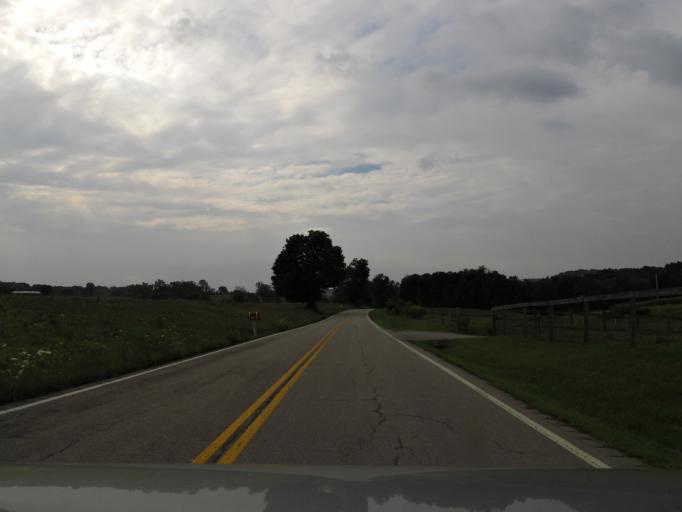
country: US
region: Kentucky
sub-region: Robertson County
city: Mount Olivet
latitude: 38.5012
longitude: -84.1367
